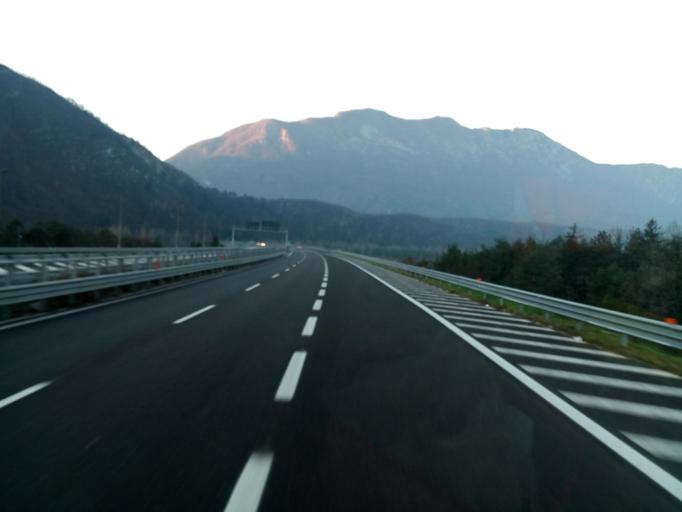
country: IT
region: Friuli Venezia Giulia
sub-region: Provincia di Udine
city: Amaro
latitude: 46.3645
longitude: 13.0766
